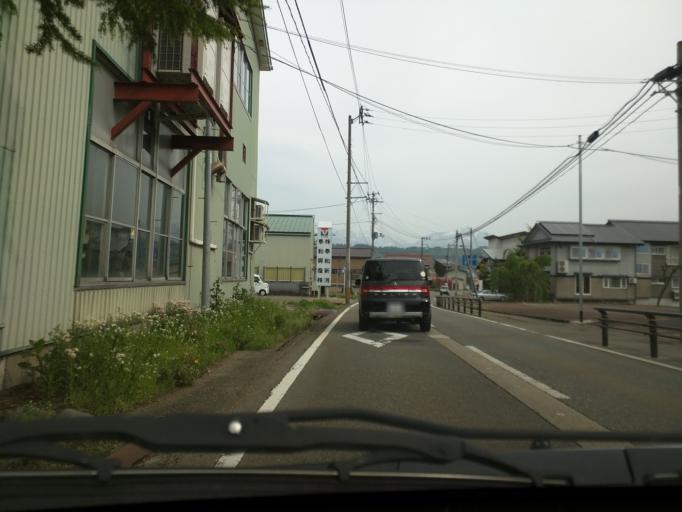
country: JP
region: Niigata
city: Ojiya
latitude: 37.2504
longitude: 138.9296
